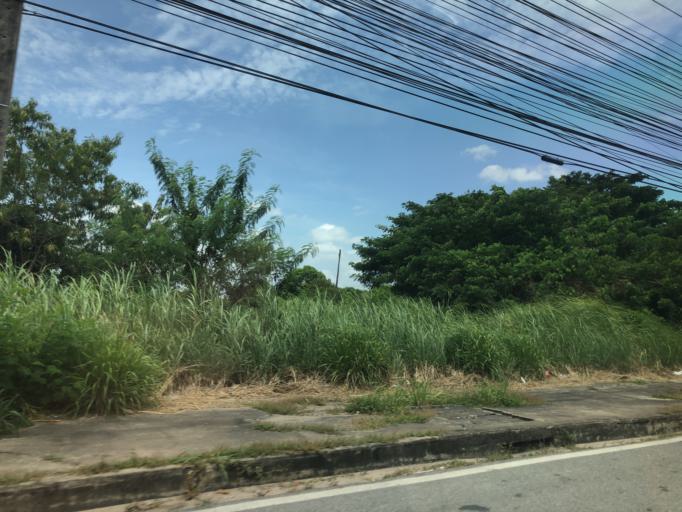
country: TH
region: Chon Buri
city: Bang Lamung
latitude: 13.0306
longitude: 100.9294
